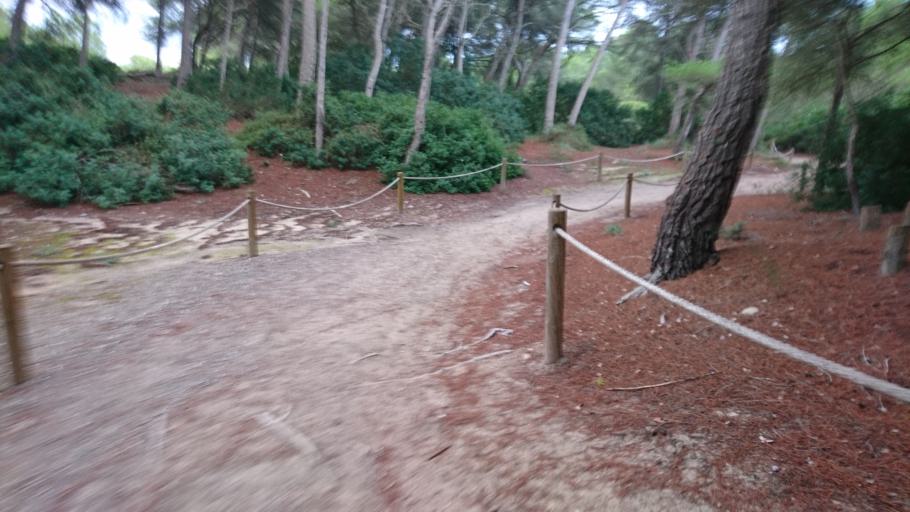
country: ES
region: Balearic Islands
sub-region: Illes Balears
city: Port d'Alcudia
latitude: 39.7795
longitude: 3.1350
